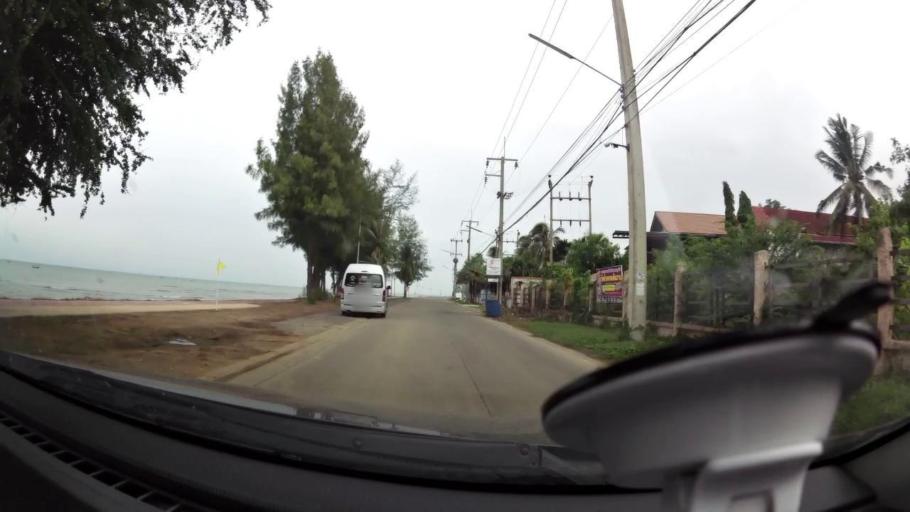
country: TH
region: Prachuap Khiri Khan
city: Pran Buri
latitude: 12.3951
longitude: 99.9957
